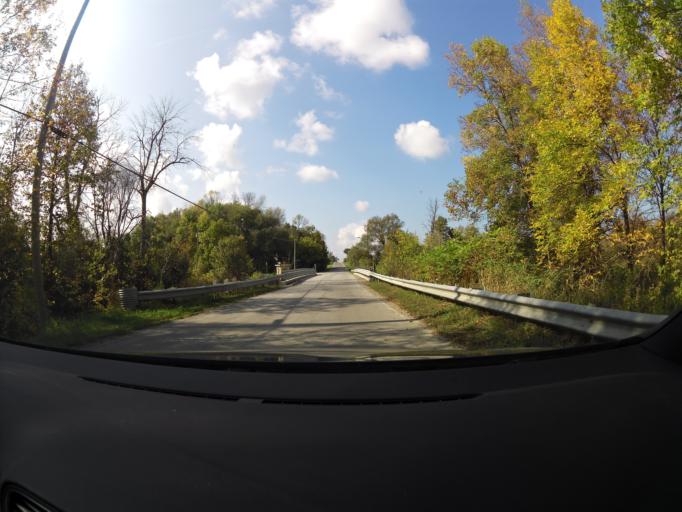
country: CA
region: Ontario
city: Arnprior
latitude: 45.4171
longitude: -76.1980
